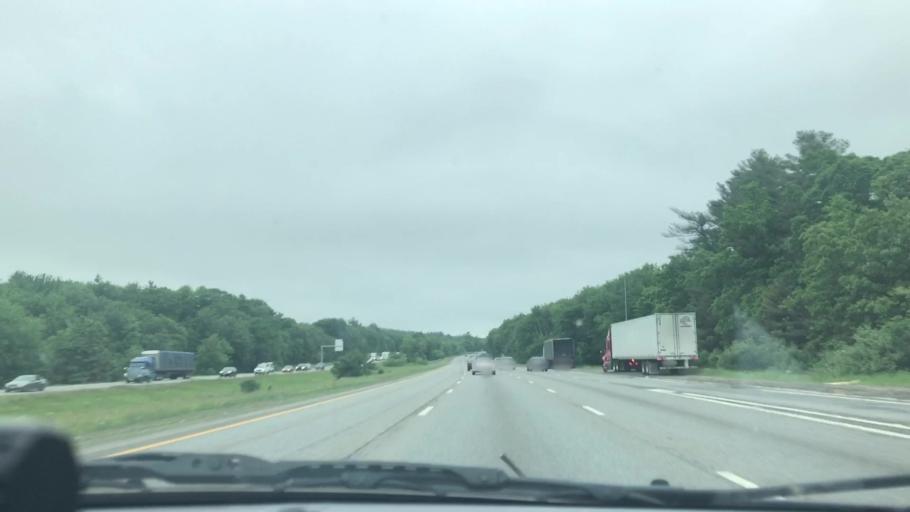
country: US
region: Massachusetts
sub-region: Worcester County
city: Bolton
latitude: 42.4341
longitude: -71.5908
